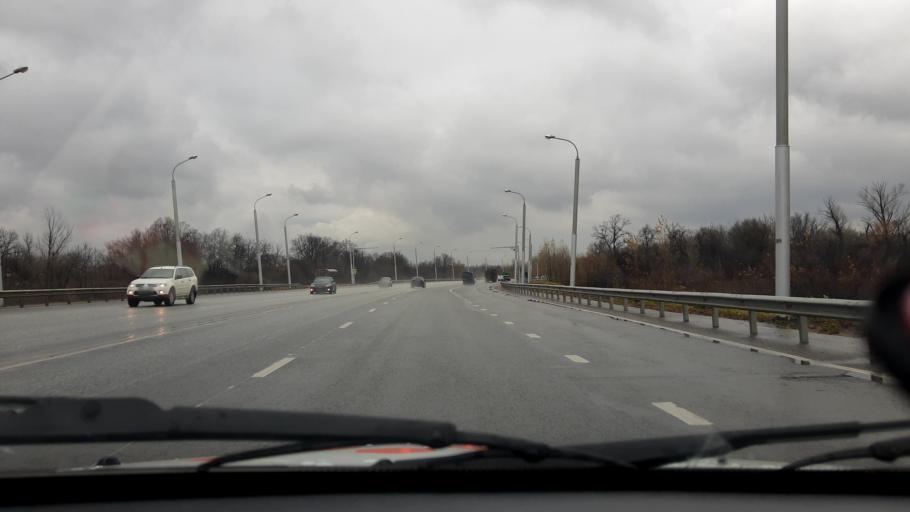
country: RU
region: Bashkortostan
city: Iglino
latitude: 54.7991
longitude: 56.2022
